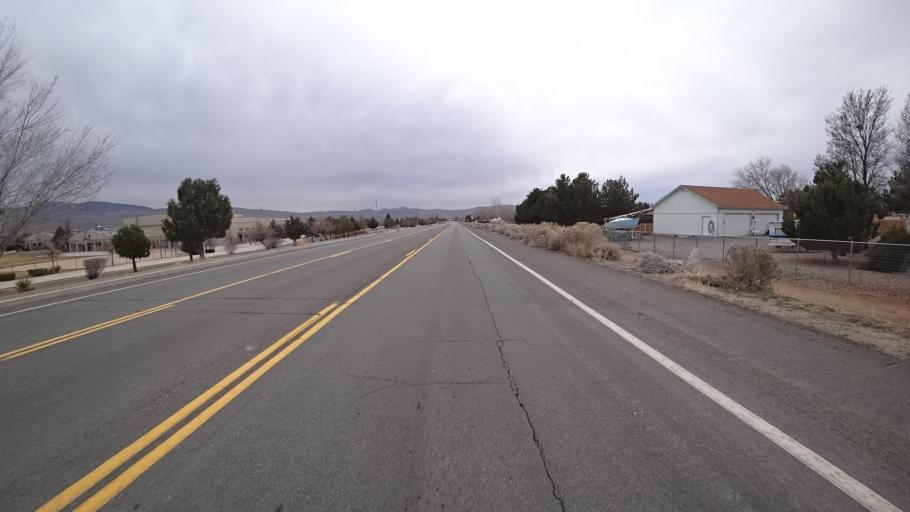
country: US
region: Nevada
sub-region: Washoe County
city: Spanish Springs
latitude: 39.6482
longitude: -119.7253
